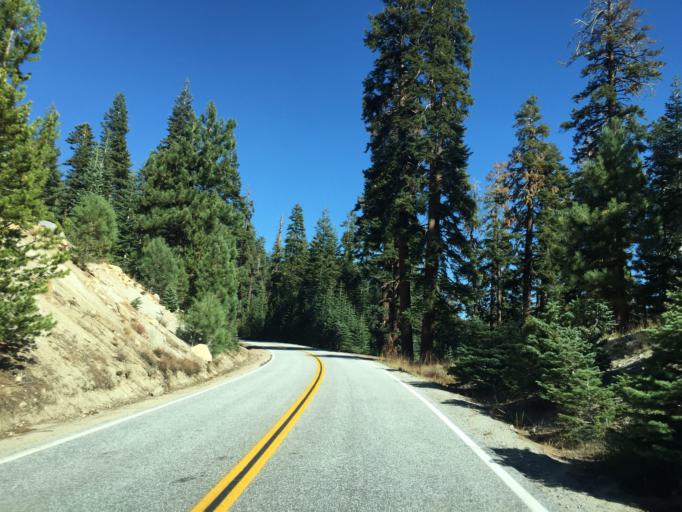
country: US
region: California
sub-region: Mariposa County
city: Yosemite Valley
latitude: 37.8063
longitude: -119.5520
